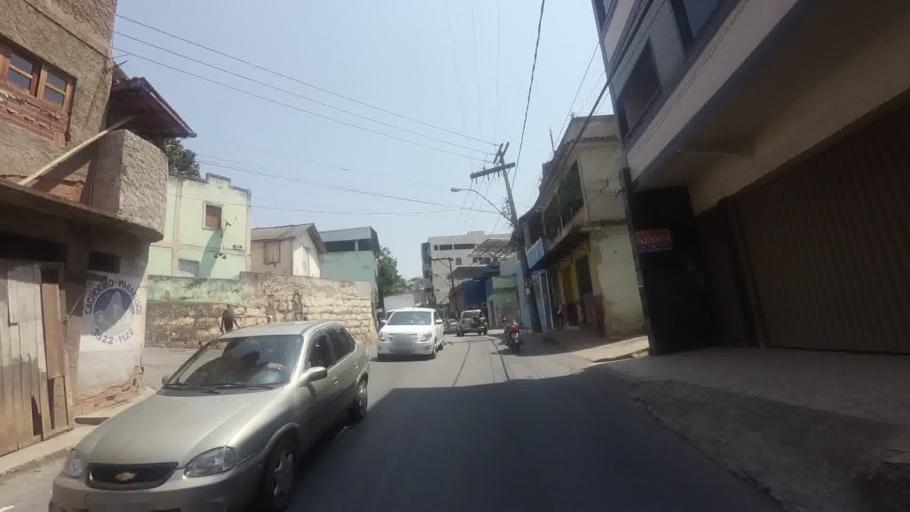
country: BR
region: Espirito Santo
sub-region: Cachoeiro De Itapemirim
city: Cachoeiro de Itapemirim
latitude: -20.8411
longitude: -41.1254
